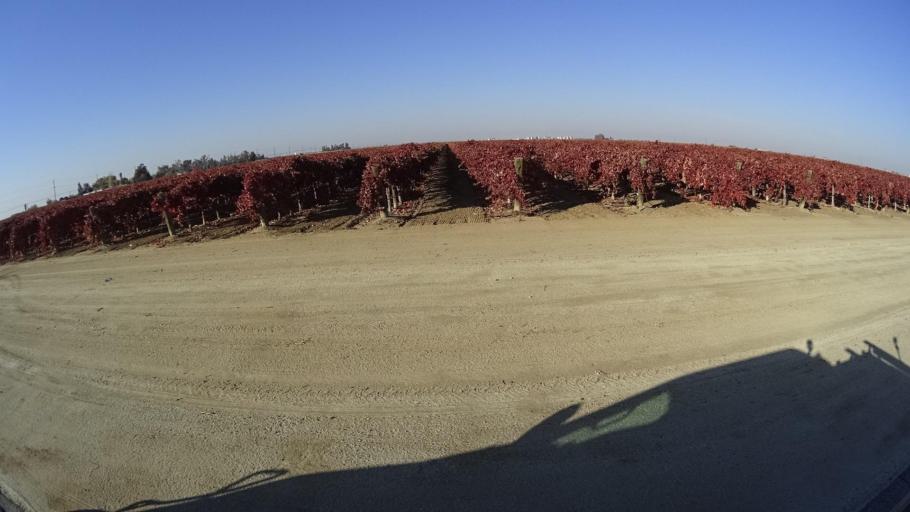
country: US
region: California
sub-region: Tulare County
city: Richgrove
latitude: 35.7785
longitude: -119.1697
